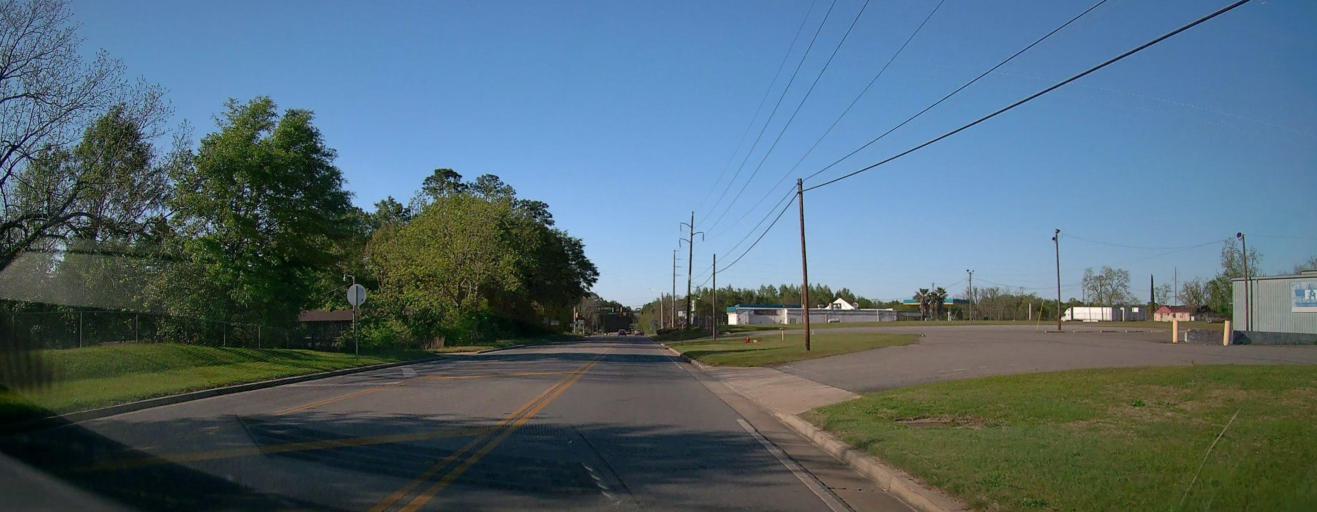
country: US
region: Georgia
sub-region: Ben Hill County
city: Fitzgerald
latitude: 31.7122
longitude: -83.2357
